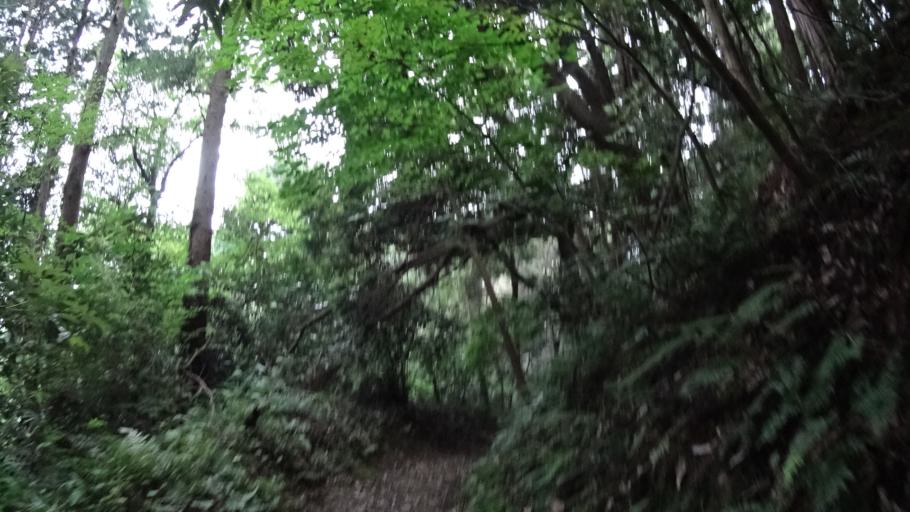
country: JP
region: Kanagawa
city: Yokosuka
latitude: 35.2868
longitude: 139.6236
